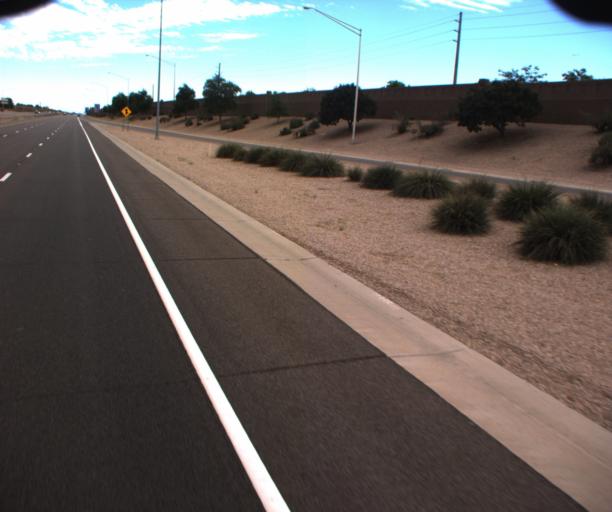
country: US
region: Arizona
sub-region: Maricopa County
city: Gilbert
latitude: 33.3278
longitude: -111.7189
